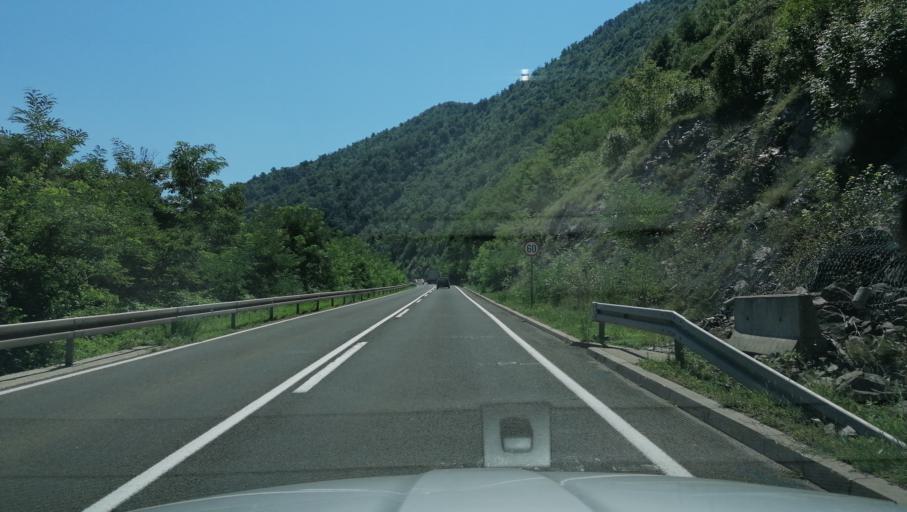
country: RS
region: Central Serbia
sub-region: Raski Okrug
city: Kraljevo
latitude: 43.5939
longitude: 20.5705
